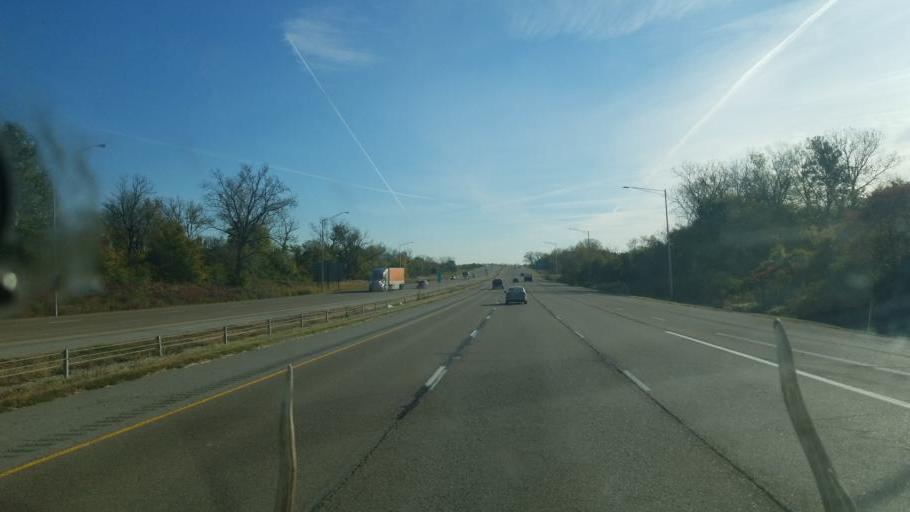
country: US
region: Illinois
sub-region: Saint Clair County
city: Fairmont City
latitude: 38.6626
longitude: -90.0900
